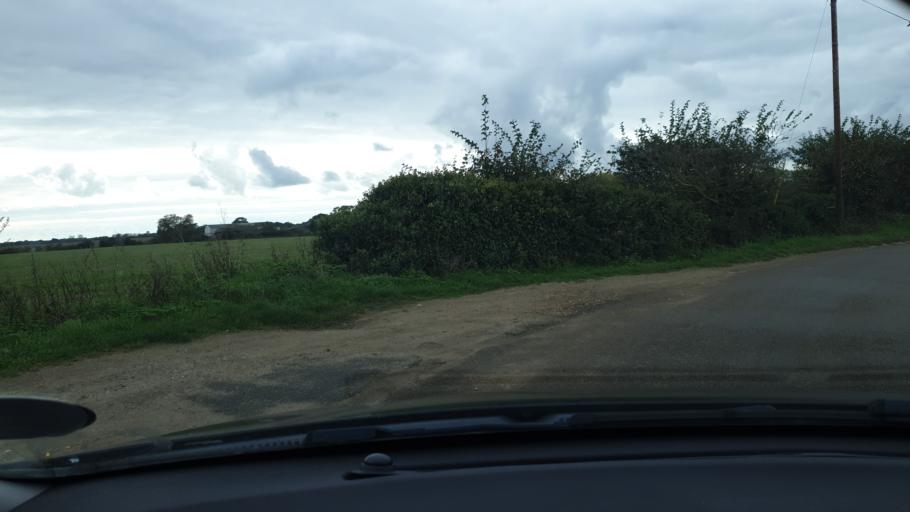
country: GB
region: England
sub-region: Essex
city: Manningtree
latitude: 51.9344
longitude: 1.0626
